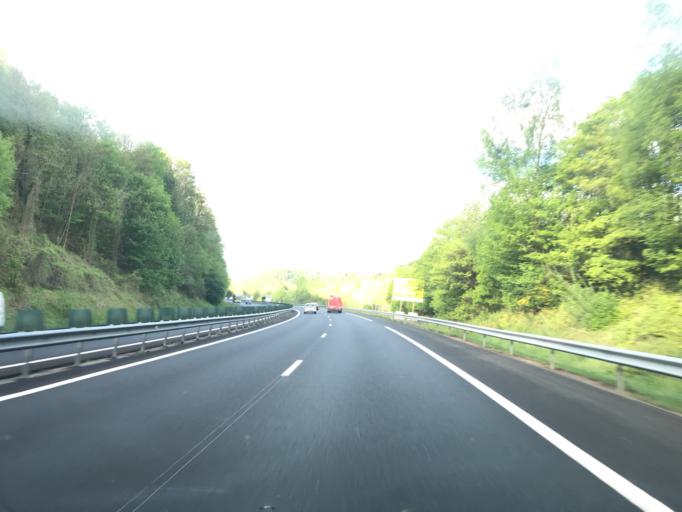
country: FR
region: Haute-Normandie
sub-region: Departement de l'Eure
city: Saint-Germain-Village
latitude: 49.3856
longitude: 0.5004
